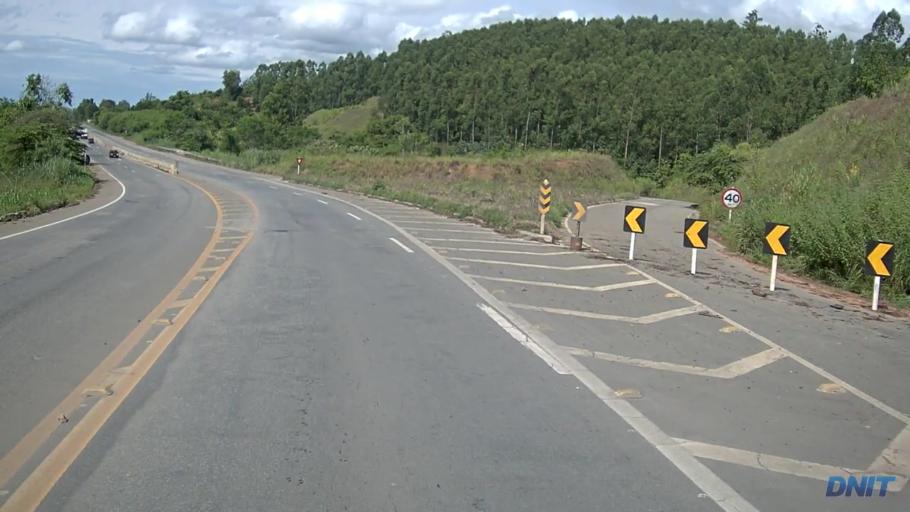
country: BR
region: Minas Gerais
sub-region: Ipaba
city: Ipaba
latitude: -19.3232
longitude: -42.4085
